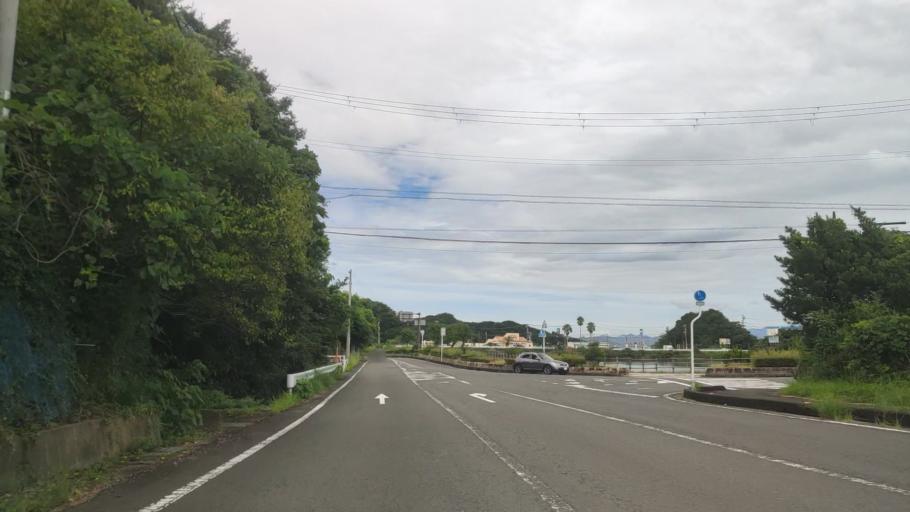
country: JP
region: Wakayama
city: Tanabe
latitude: 33.6907
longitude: 135.3879
